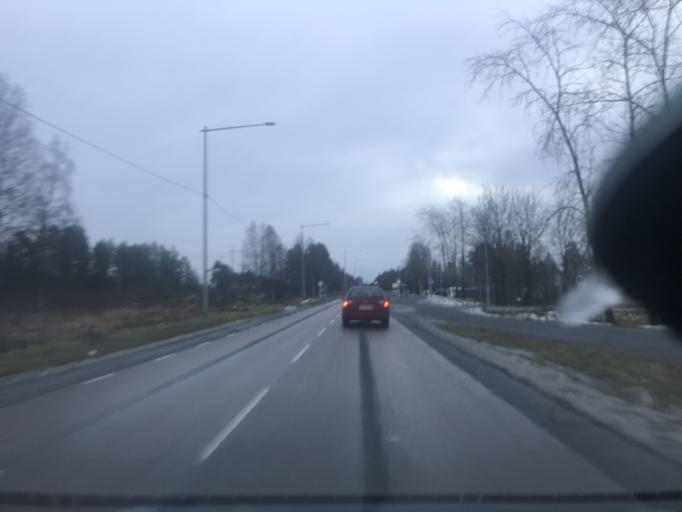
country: SE
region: Norrbotten
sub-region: Lulea Kommun
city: Gammelstad
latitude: 65.6360
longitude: 22.0291
